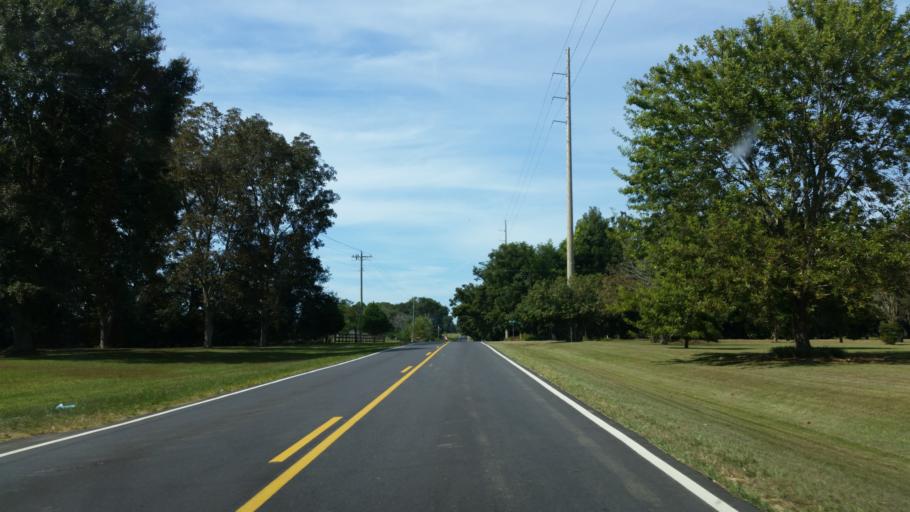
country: US
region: Alabama
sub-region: Baldwin County
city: Loxley
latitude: 30.6331
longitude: -87.7327
